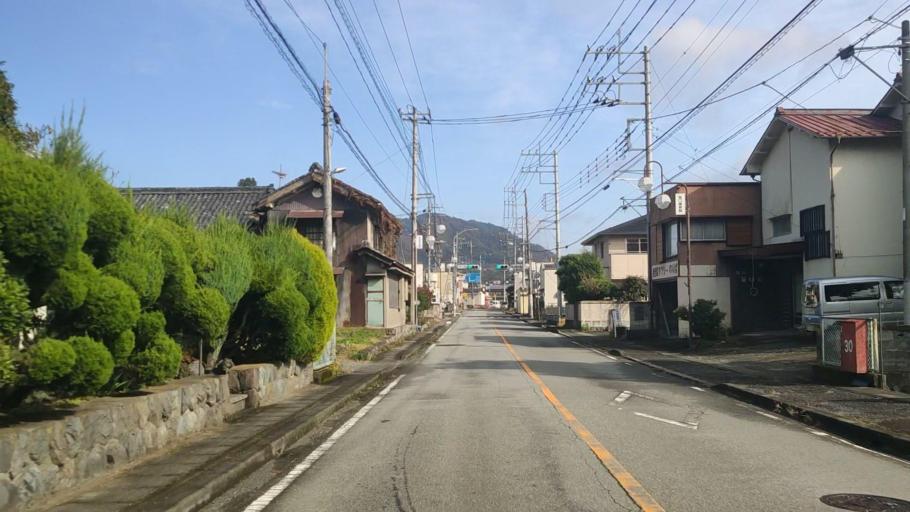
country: JP
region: Yamanashi
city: Ryuo
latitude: 35.4853
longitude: 138.4476
